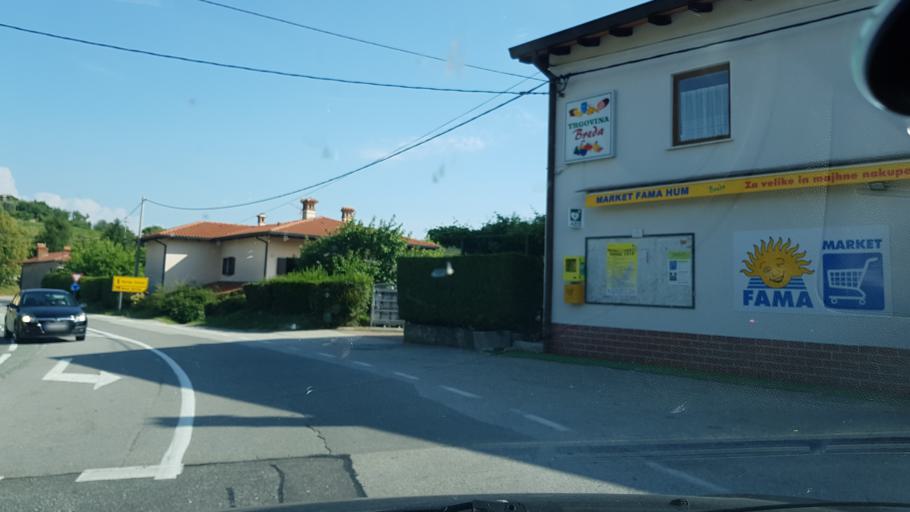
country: IT
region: Friuli Venezia Giulia
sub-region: Provincia di Gorizia
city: San Floriano del Collio
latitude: 45.9964
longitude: 13.5799
